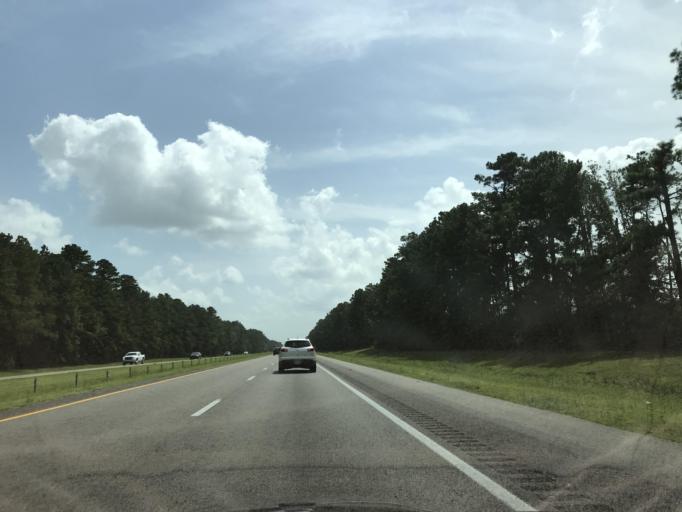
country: US
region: North Carolina
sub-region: Pender County
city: Rocky Point
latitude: 34.4971
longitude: -77.8772
